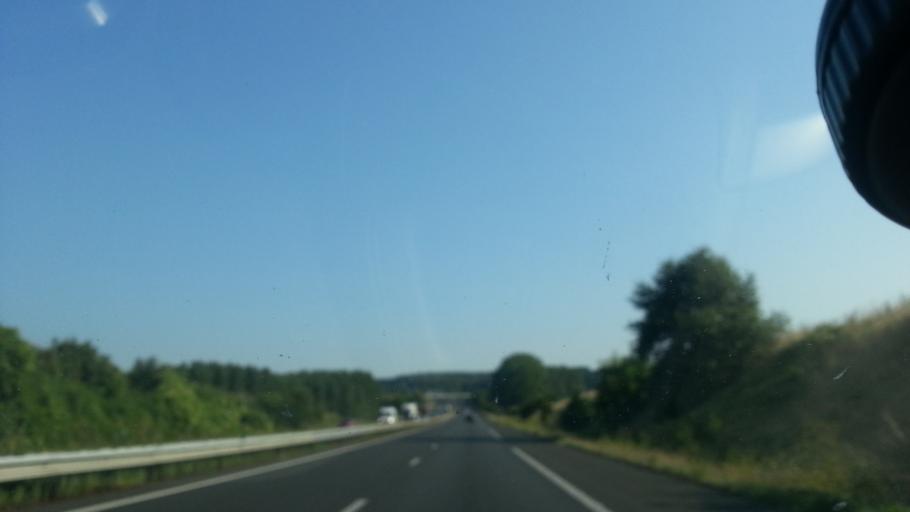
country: FR
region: Poitou-Charentes
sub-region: Departement de la Vienne
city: Dange-Saint-Romain
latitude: 46.9445
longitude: 0.5471
